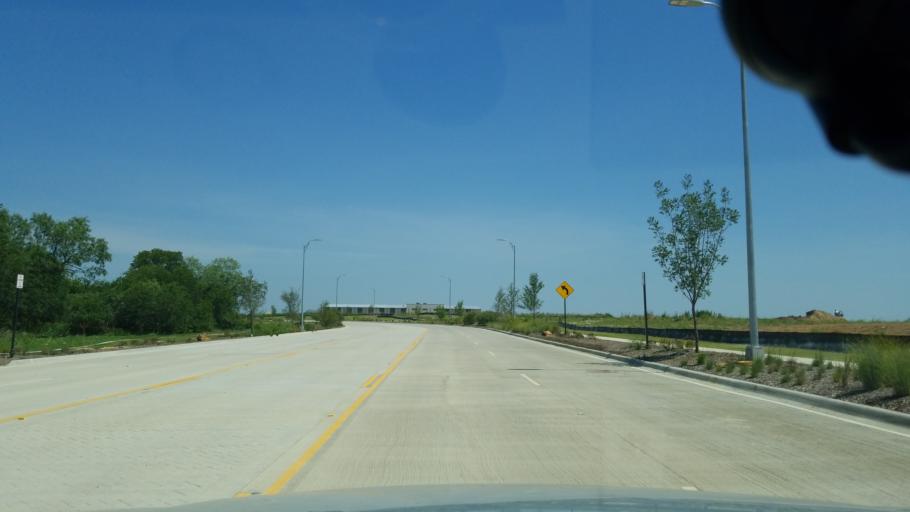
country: US
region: Texas
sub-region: Tarrant County
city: Euless
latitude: 32.8472
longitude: -97.0309
